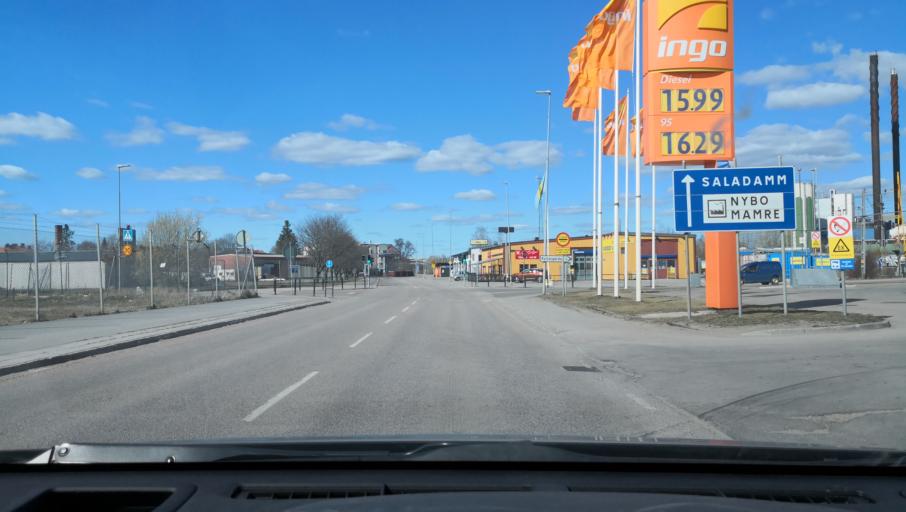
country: SE
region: Vaestmanland
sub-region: Sala Kommun
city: Sala
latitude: 59.9181
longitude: 16.6161
